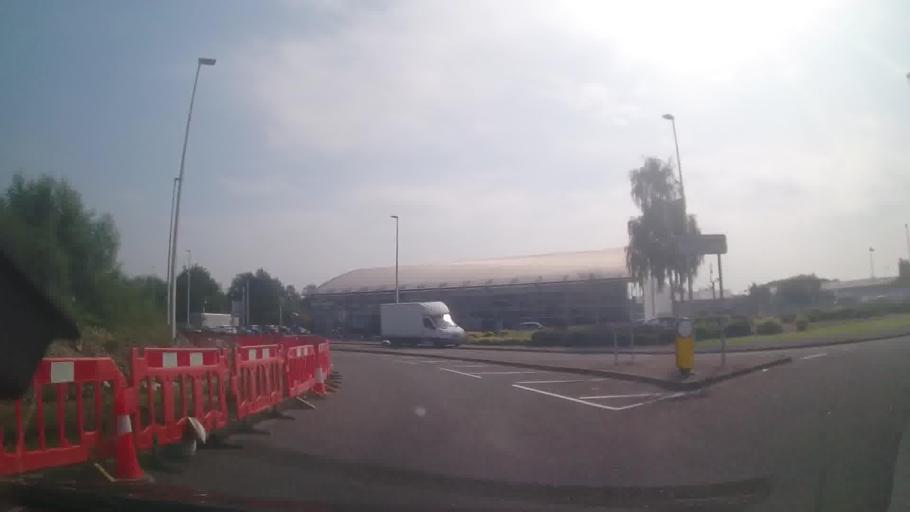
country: GB
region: England
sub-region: Warrington
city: Great Sankey
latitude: 53.4142
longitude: -2.6349
